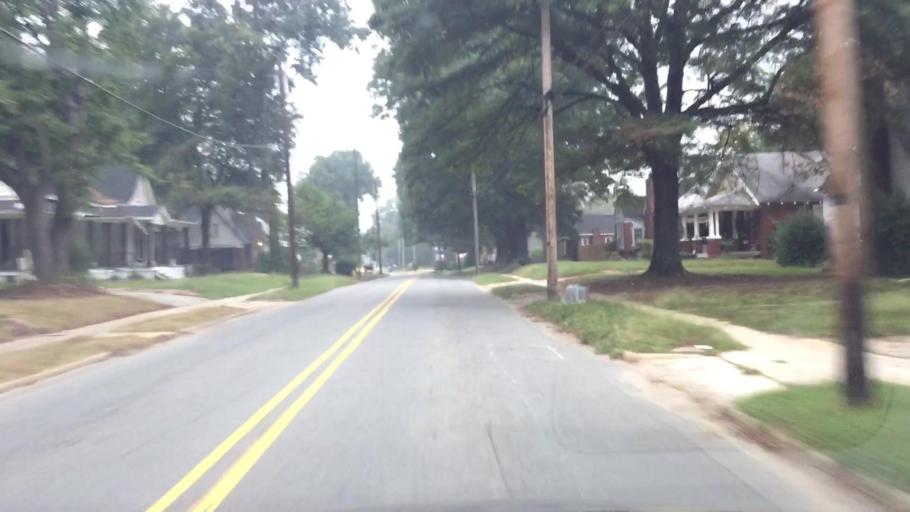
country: US
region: North Carolina
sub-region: Iredell County
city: Mooresville
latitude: 35.5905
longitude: -80.8051
